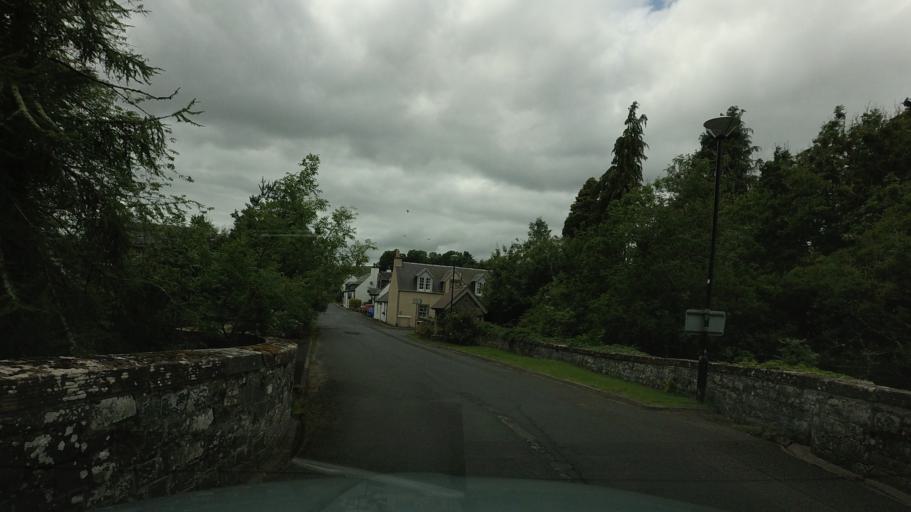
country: GB
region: Scotland
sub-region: The Scottish Borders
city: Selkirk
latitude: 55.5084
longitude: -2.9671
